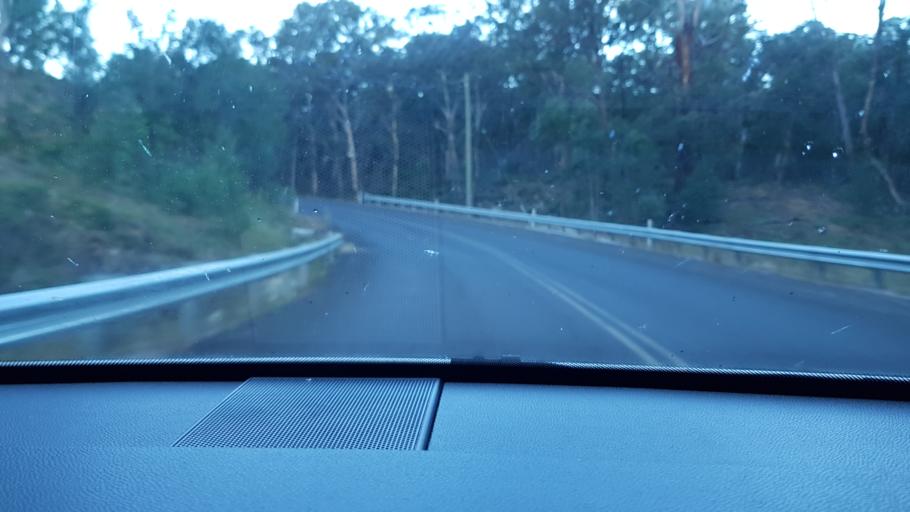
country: AU
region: New South Wales
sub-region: Lithgow
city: Portland
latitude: -33.2636
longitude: 150.1270
